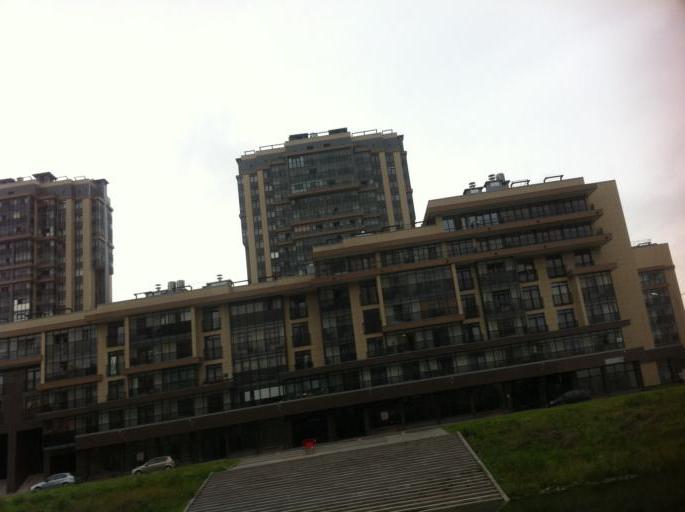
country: RU
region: St.-Petersburg
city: Sosnovaya Polyana
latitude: 59.8535
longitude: 30.1445
